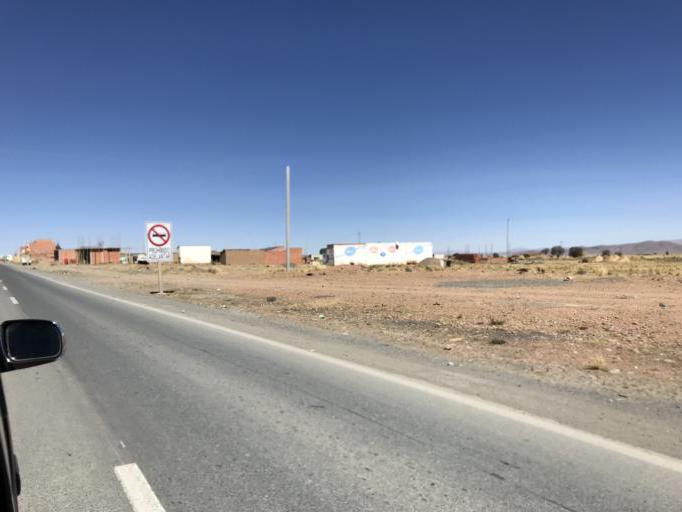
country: BO
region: La Paz
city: Batallas
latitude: -16.3318
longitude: -68.4202
